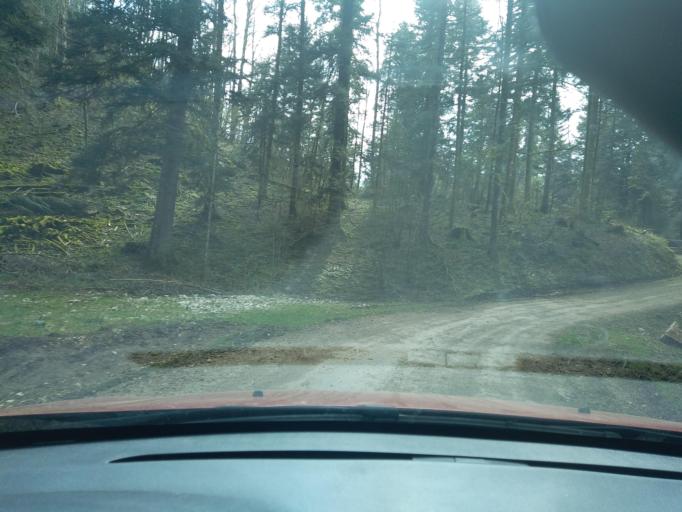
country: FR
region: Franche-Comte
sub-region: Departement du Jura
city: Moirans-en-Montagne
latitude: 46.4736
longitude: 5.7591
